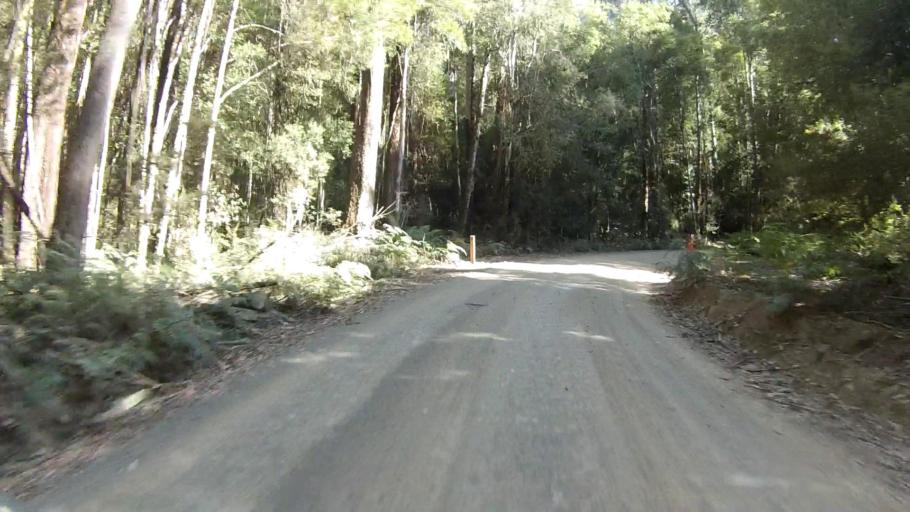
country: AU
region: Tasmania
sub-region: Derwent Valley
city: New Norfolk
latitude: -42.6818
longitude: 146.7024
